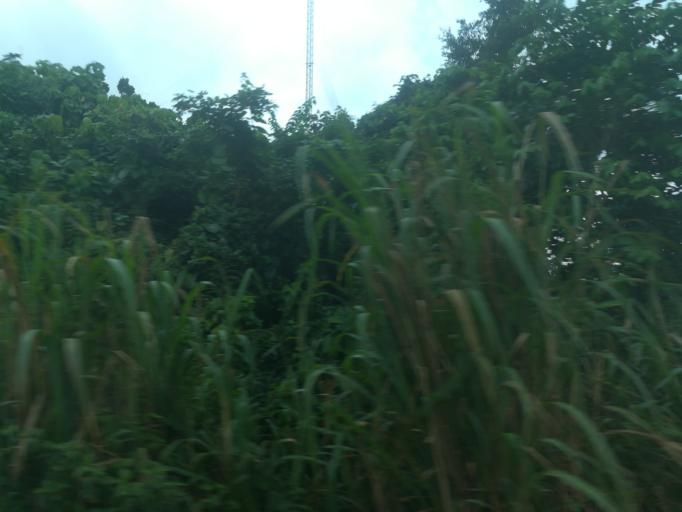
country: NG
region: Lagos
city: Ikorodu
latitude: 6.6636
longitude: 3.6209
